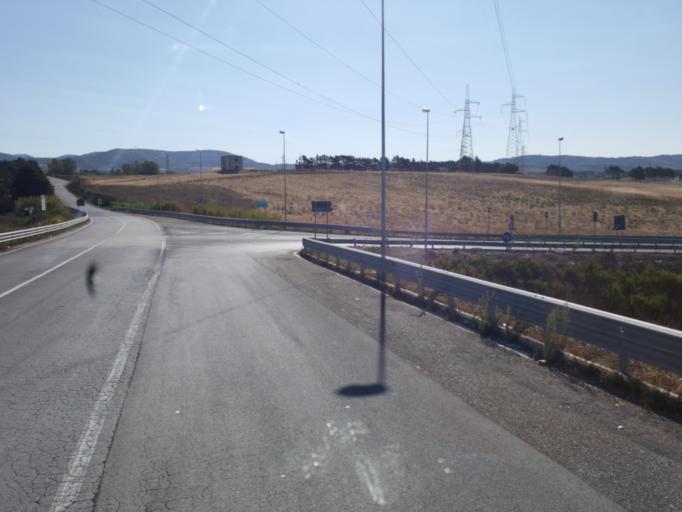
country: IT
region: Latium
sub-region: Citta metropolitana di Roma Capitale
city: Aurelia
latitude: 42.1295
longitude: 11.7933
